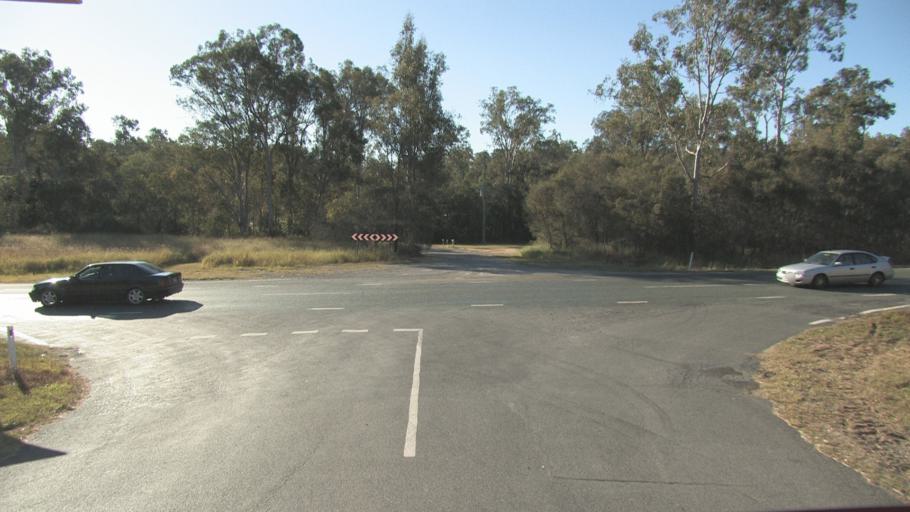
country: AU
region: Queensland
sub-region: Logan
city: North Maclean
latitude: -27.8103
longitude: 153.0408
